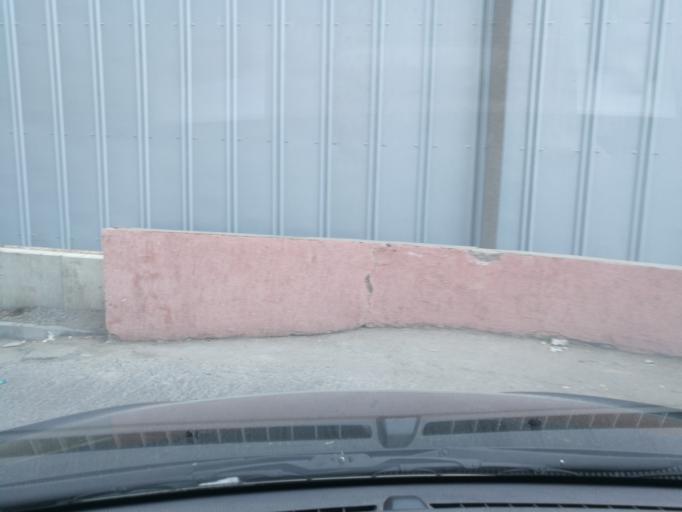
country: MN
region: Ulaanbaatar
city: Ulaanbaatar
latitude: 47.8999
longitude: 106.9209
